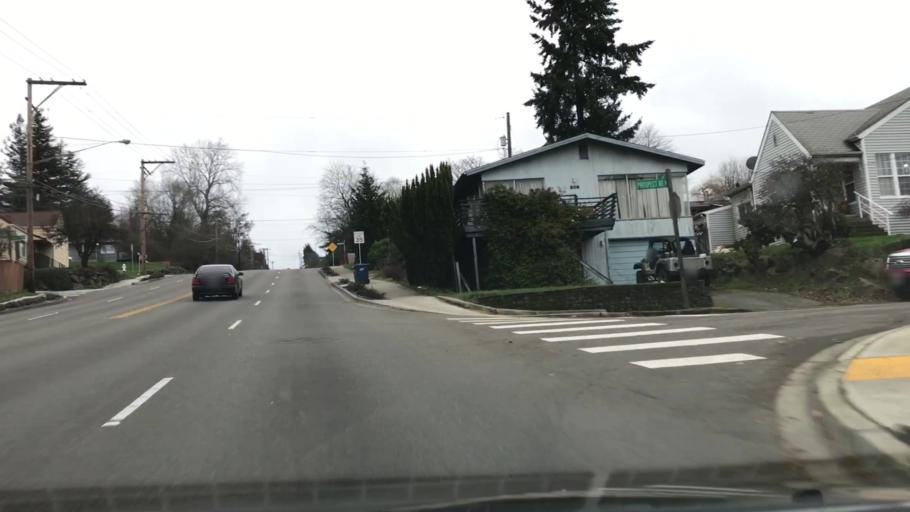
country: US
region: Washington
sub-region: King County
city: Kent
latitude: 47.3866
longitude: -122.2246
